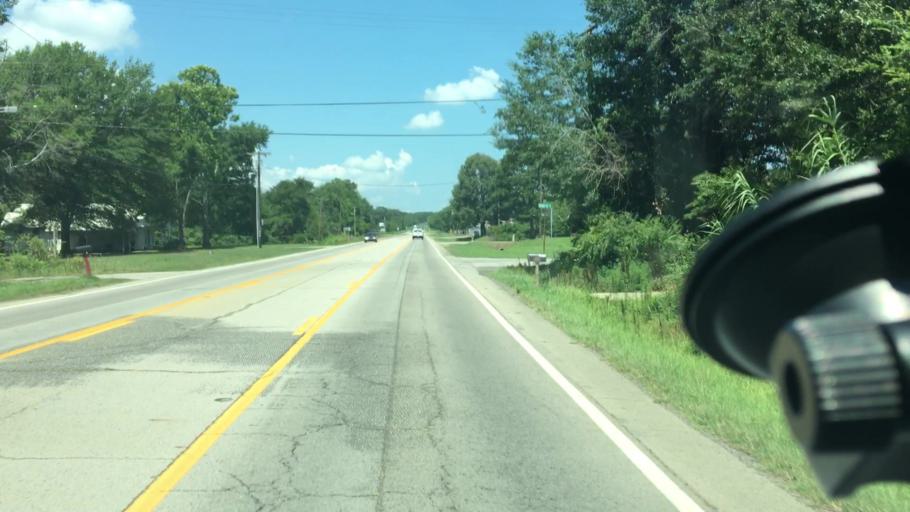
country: US
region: Arkansas
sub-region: Sebastian County
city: Lavaca
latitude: 35.2949
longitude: -94.1428
